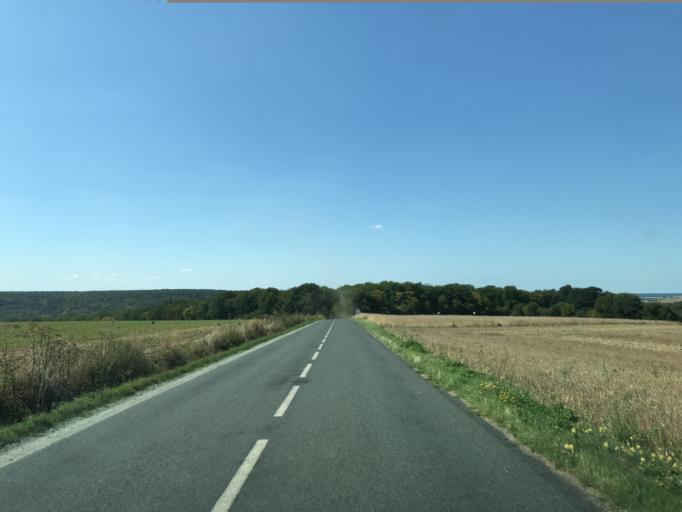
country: FR
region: Haute-Normandie
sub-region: Departement de l'Eure
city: Houlbec-Cocherel
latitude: 49.0830
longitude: 1.3128
